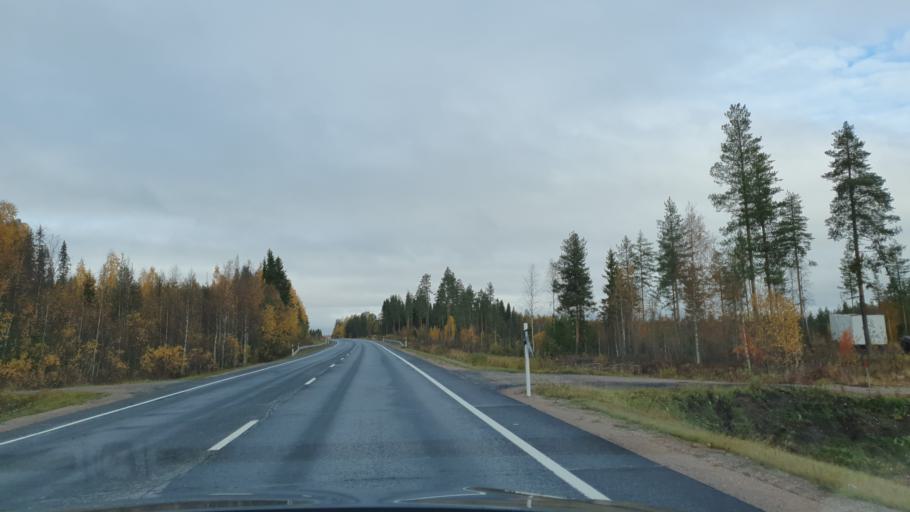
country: FI
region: Lapland
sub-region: Rovaniemi
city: Rovaniemi
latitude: 66.6187
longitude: 25.5434
